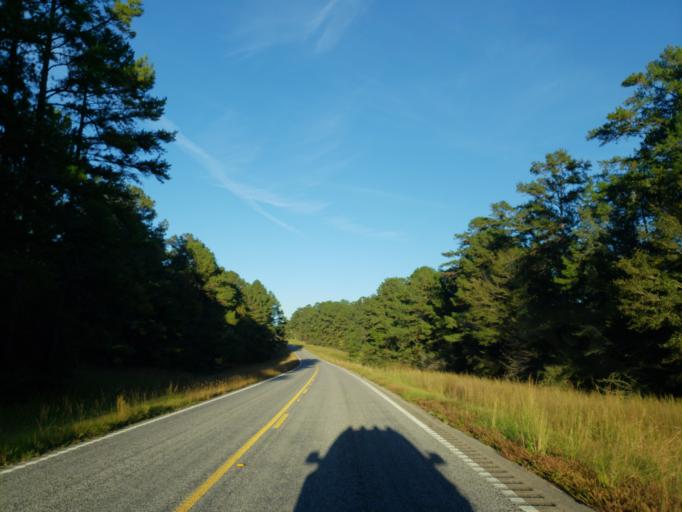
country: US
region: Mississippi
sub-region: Wayne County
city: Belmont
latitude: 31.4026
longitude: -88.6250
